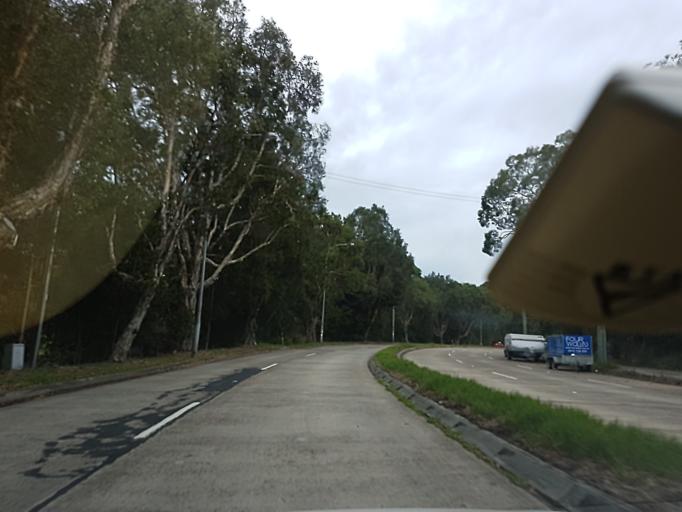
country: AU
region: New South Wales
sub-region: Warringah
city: North Manly
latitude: -33.7732
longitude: 151.2682
